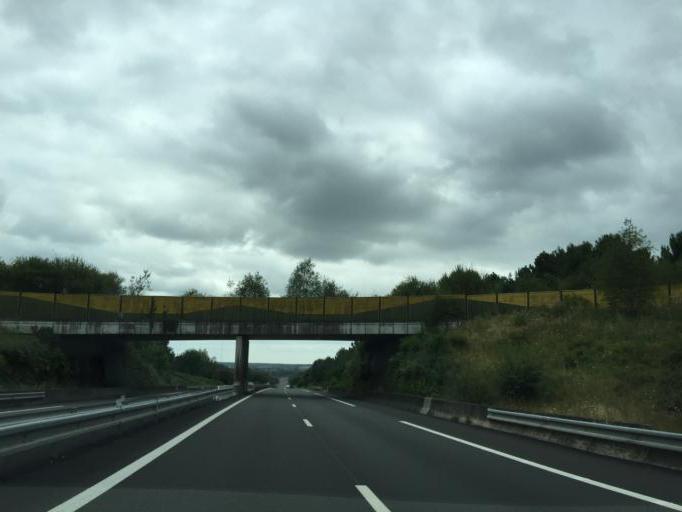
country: FR
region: Pays de la Loire
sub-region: Departement de la Sarthe
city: Ecommoy
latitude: 47.8396
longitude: 0.3055
